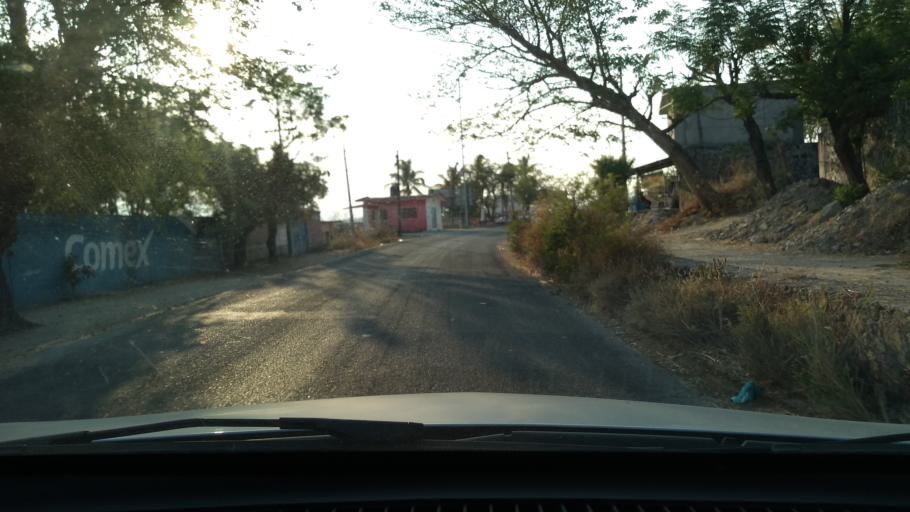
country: MX
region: Morelos
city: Puente de Ixtla
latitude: 18.6072
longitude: -99.3172
